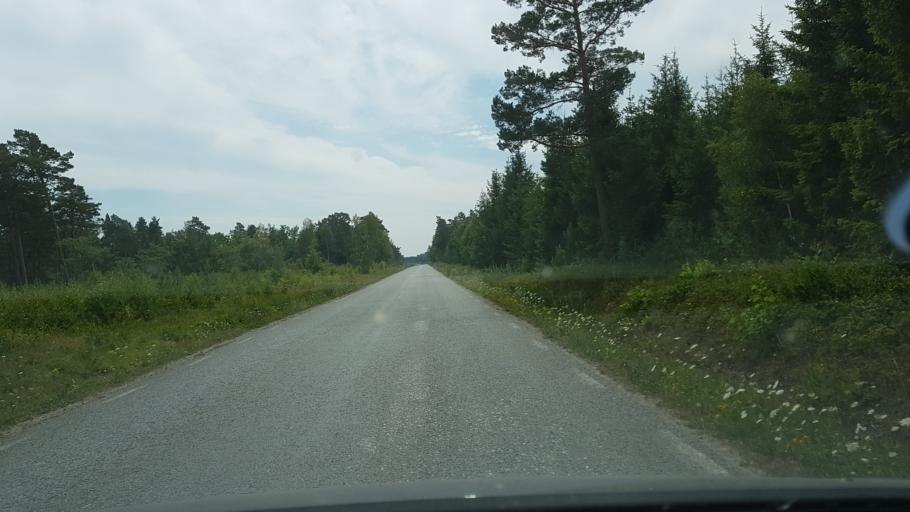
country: SE
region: Gotland
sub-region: Gotland
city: Visby
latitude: 57.7124
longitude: 18.5077
